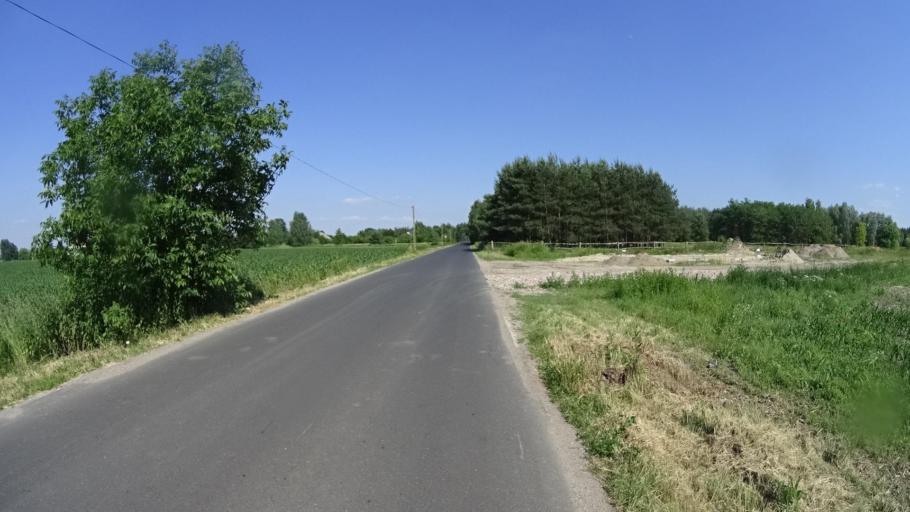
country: PL
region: Masovian Voivodeship
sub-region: Powiat warszawski zachodni
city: Blonie
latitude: 52.1653
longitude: 20.6312
